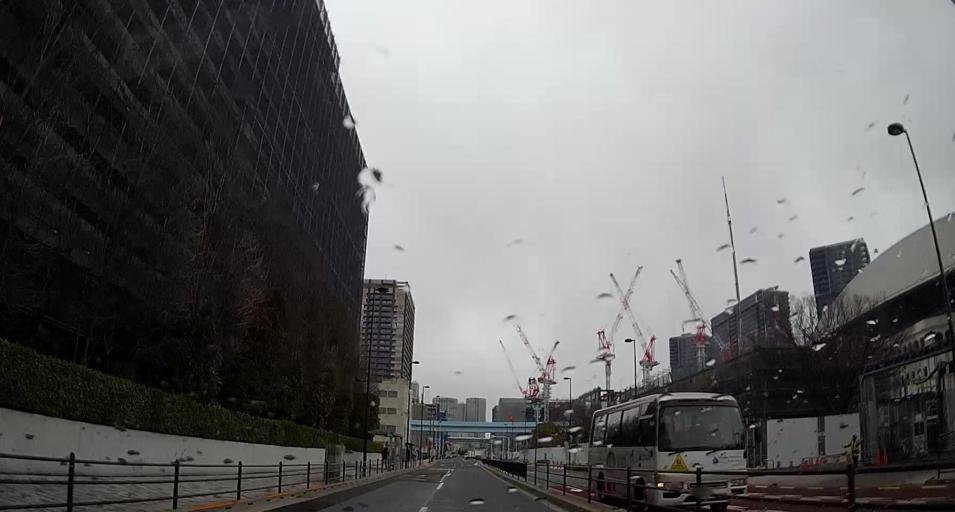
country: JP
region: Tokyo
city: Urayasu
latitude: 35.6371
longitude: 139.7886
